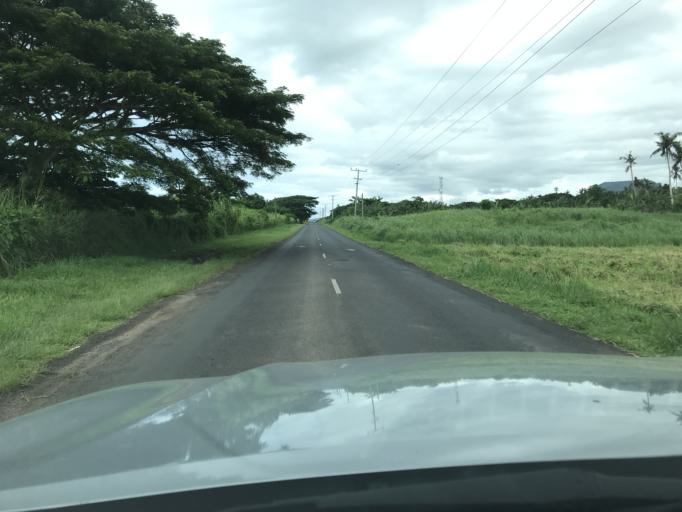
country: WS
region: Aiga-i-le-Tai
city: Mulifanua
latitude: -13.8330
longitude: -172.0240
